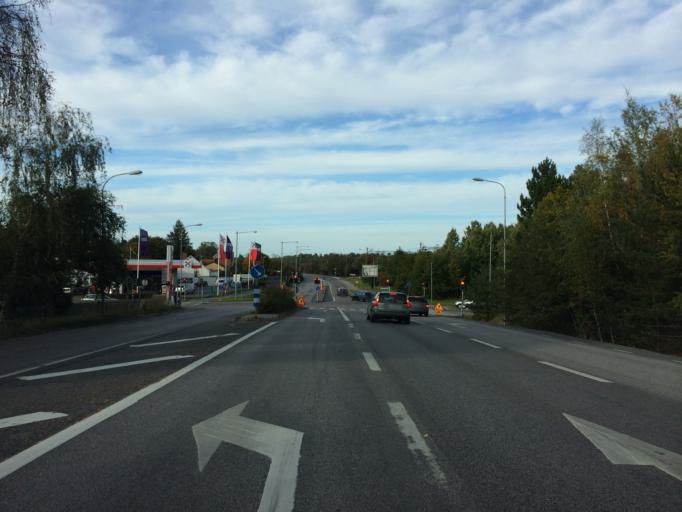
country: SE
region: Stockholm
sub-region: Sollentuna Kommun
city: Sollentuna
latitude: 59.4500
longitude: 17.9253
